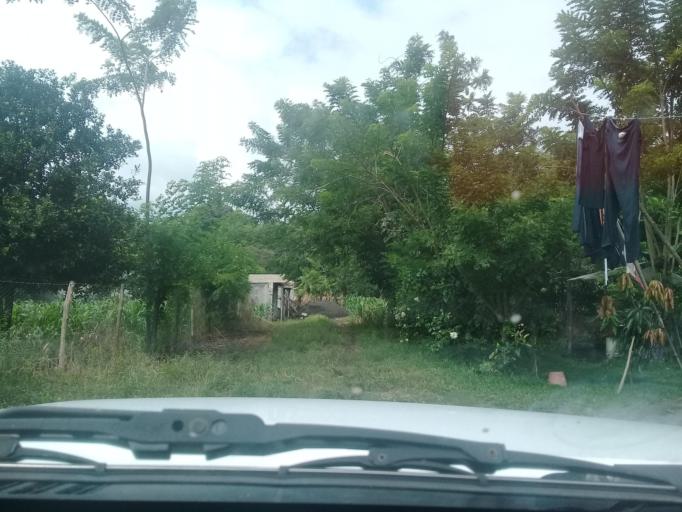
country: MX
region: Veracruz
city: Comoapan
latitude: 18.4101
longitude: -95.1597
